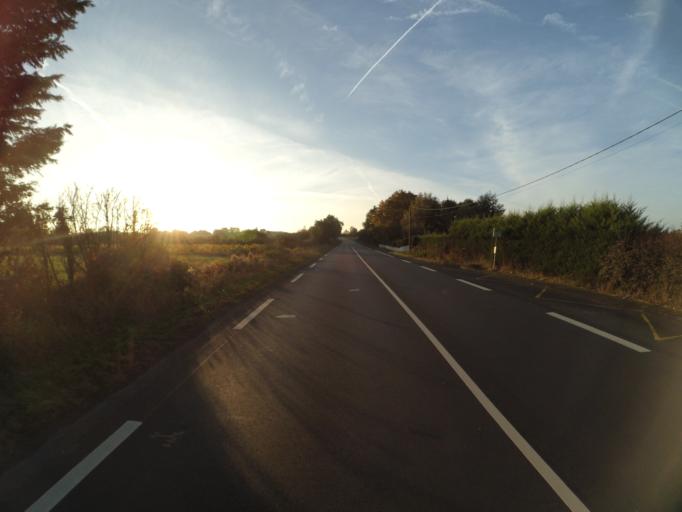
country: FR
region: Pays de la Loire
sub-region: Departement de la Loire-Atlantique
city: Le Bignon
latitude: 47.1087
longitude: -1.4718
